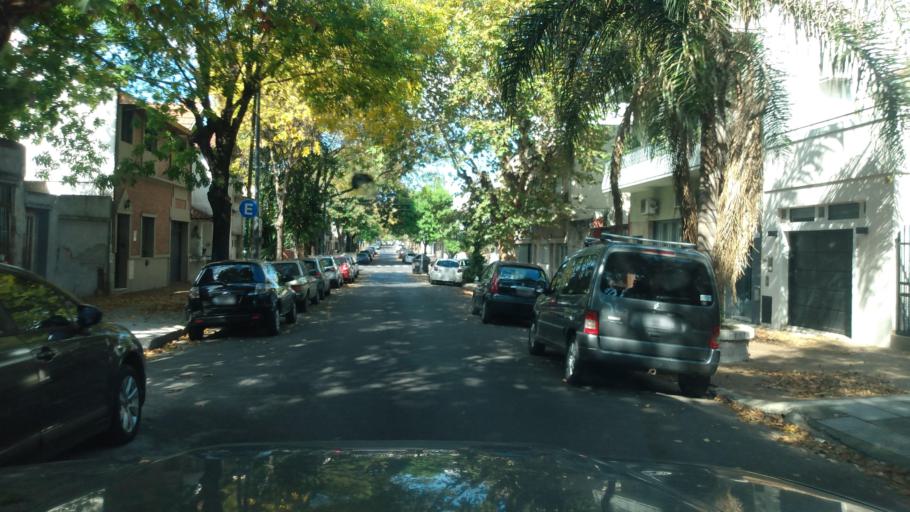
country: AR
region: Buenos Aires F.D.
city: Villa Santa Rita
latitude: -34.5834
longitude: -58.4859
